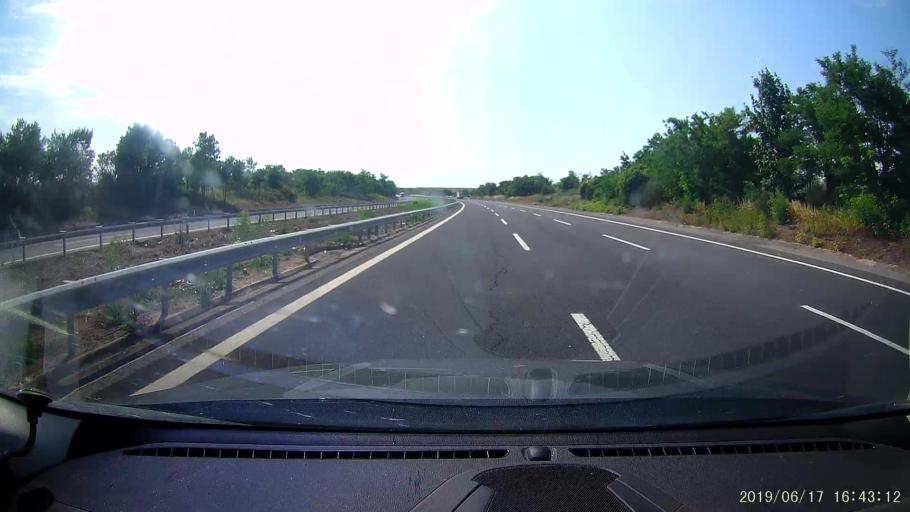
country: TR
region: Kirklareli
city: Luleburgaz
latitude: 41.4796
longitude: 27.3008
